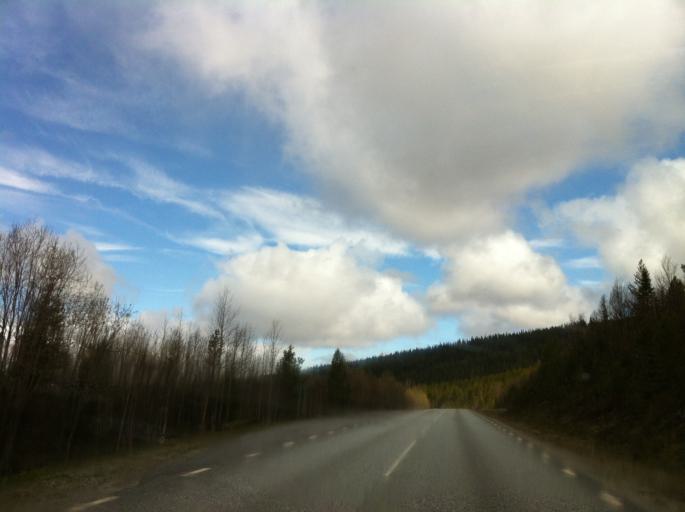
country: SE
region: Jaemtland
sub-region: Are Kommun
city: Are
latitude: 62.5765
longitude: 12.5594
